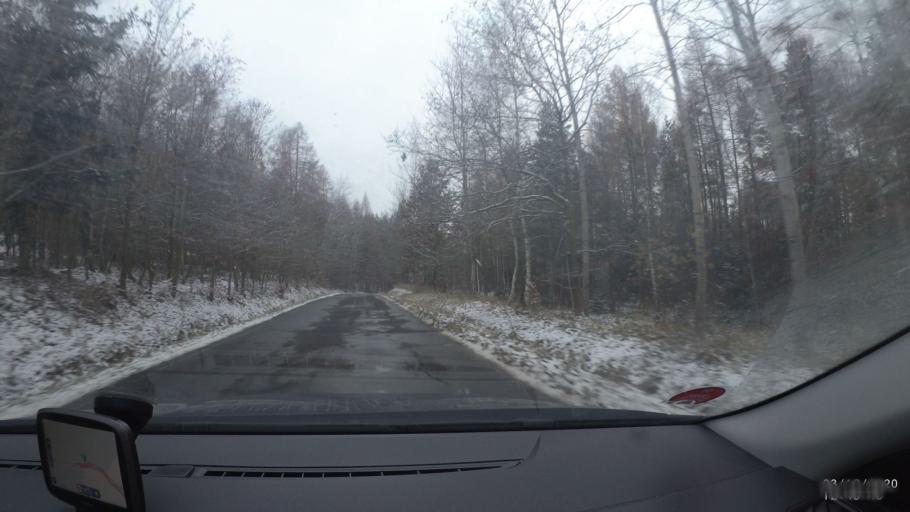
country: CZ
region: Central Bohemia
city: Nove Straseci
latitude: 50.1671
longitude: 13.8706
